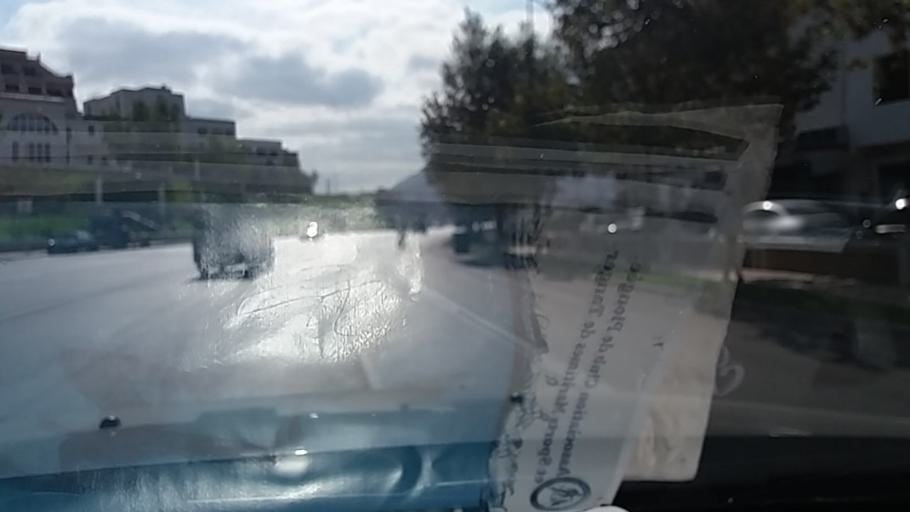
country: MA
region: Tanger-Tetouan
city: Tetouan
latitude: 35.5670
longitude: -5.4041
